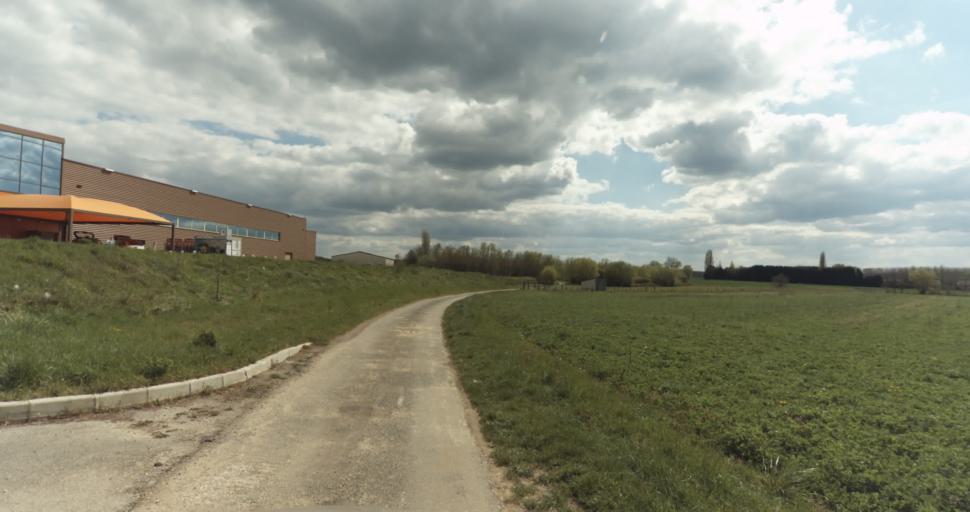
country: FR
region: Bourgogne
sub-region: Departement de la Cote-d'Or
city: Auxonne
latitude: 47.1794
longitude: 5.3988
